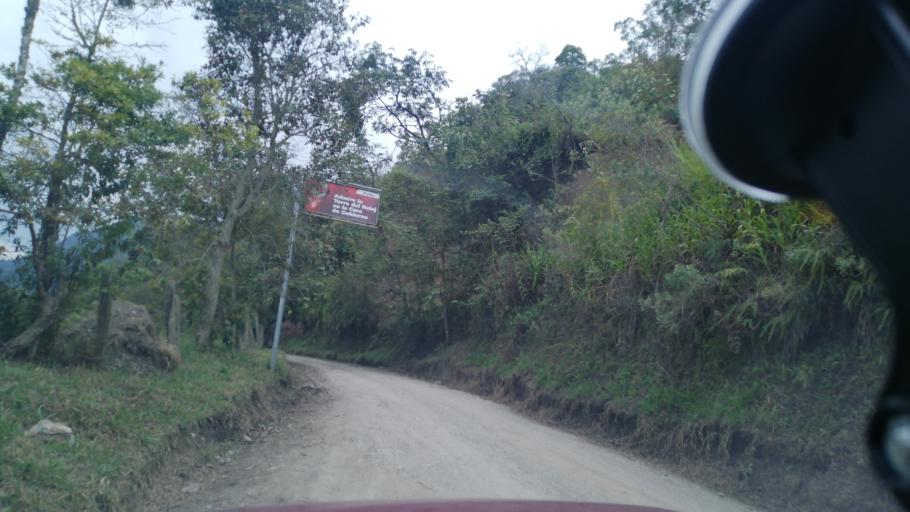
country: CO
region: Cundinamarca
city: Vergara
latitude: 5.1597
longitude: -74.2582
